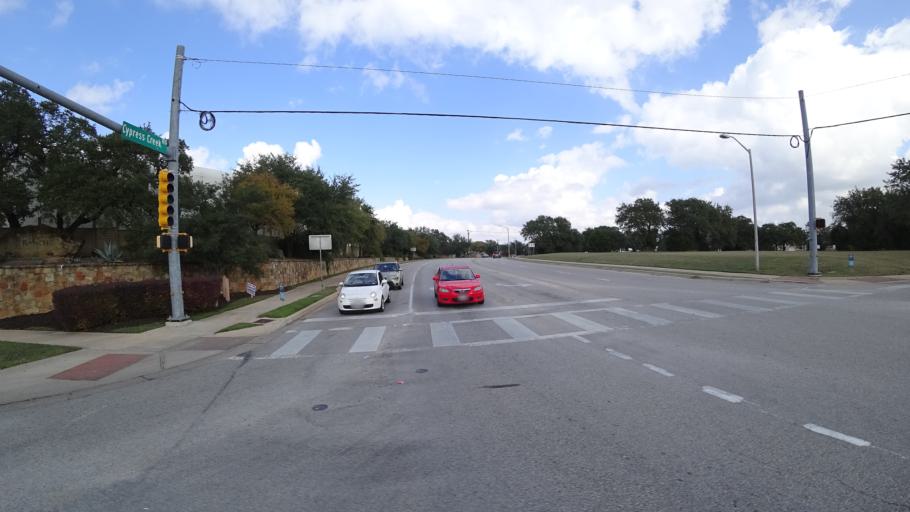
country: US
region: Texas
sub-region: Williamson County
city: Cedar Park
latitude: 30.4723
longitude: -97.8475
